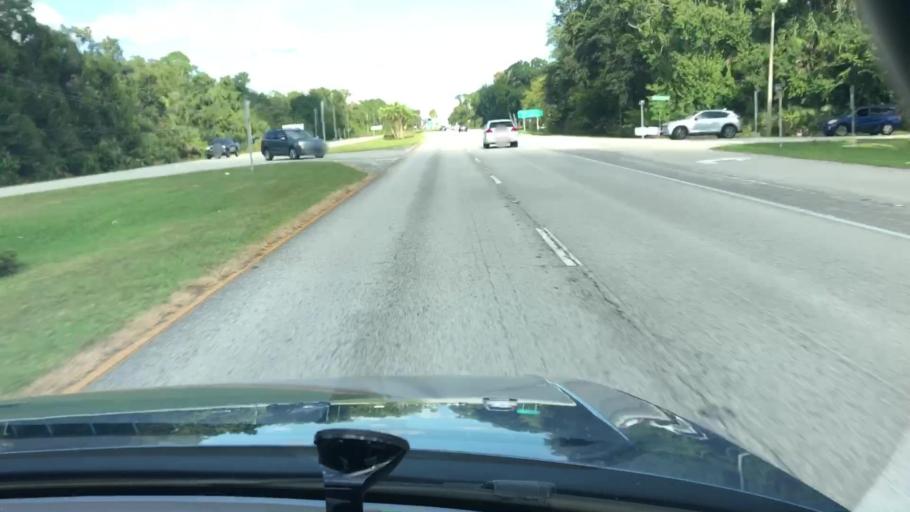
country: US
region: Florida
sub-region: Volusia County
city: South Daytona
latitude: 29.1664
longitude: -81.0495
